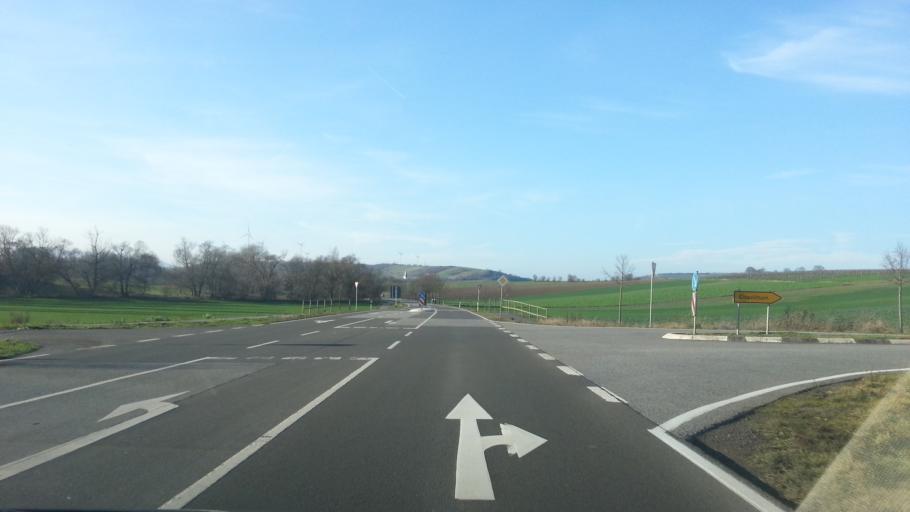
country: DE
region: Rheinland-Pfalz
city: Einselthum
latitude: 49.6476
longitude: 8.1196
